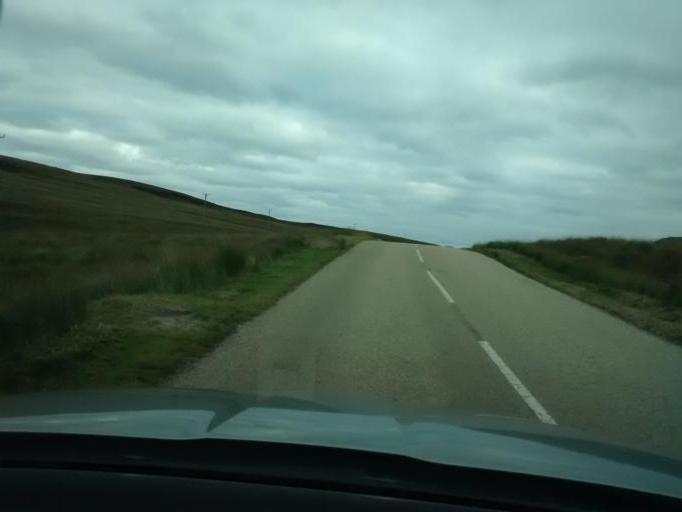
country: GB
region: Scotland
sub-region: North Ayrshire
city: Isle of Arran
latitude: 55.6880
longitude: -5.2304
